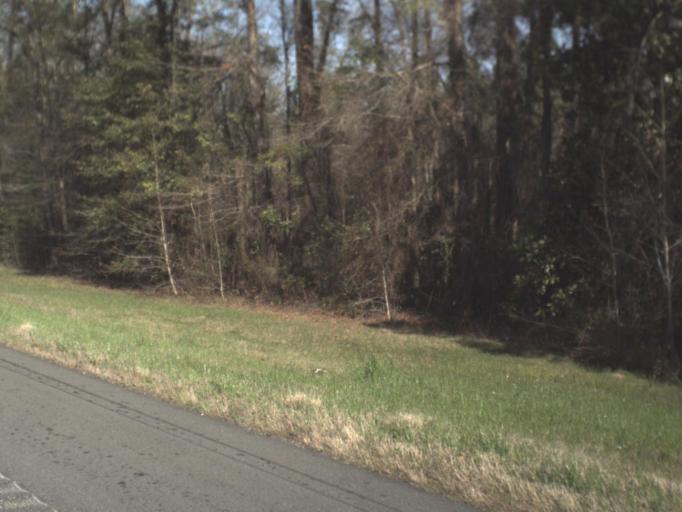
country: US
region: Florida
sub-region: Gadsden County
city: Gretna
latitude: 30.6054
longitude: -84.7385
